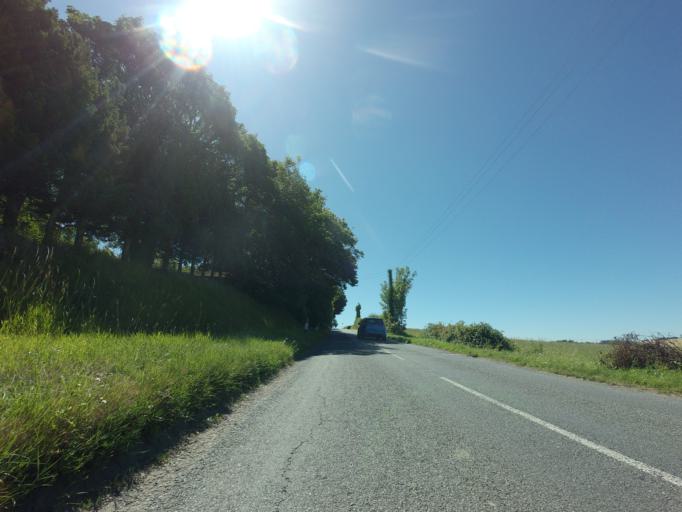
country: GB
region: England
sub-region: Kent
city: Eastry
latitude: 51.2390
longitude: 1.3075
